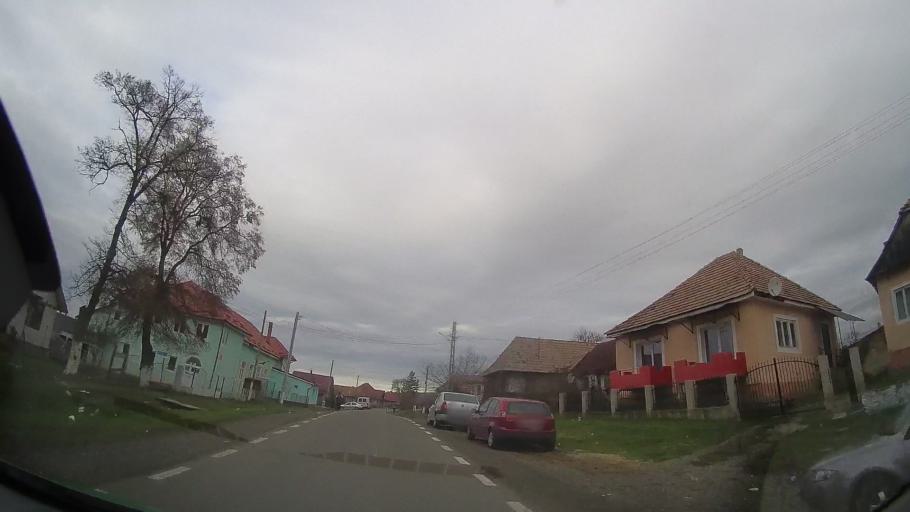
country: RO
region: Mures
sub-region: Comuna Faragau
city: Faragau
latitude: 46.7810
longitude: 24.5519
